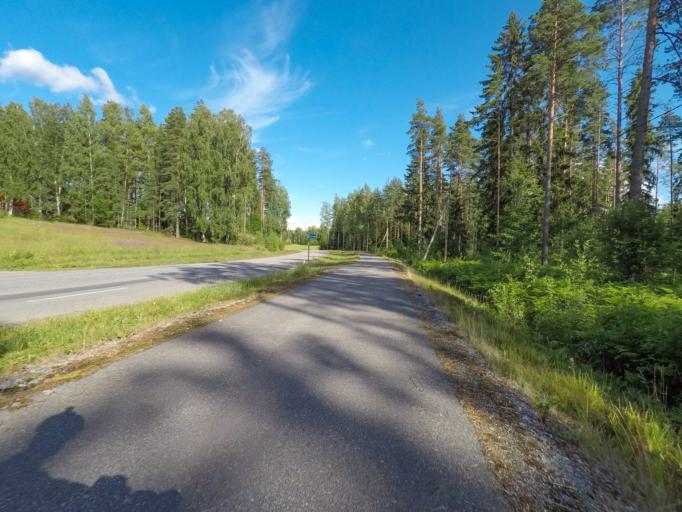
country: FI
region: South Karelia
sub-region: Lappeenranta
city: Joutseno
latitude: 61.1534
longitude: 28.5868
